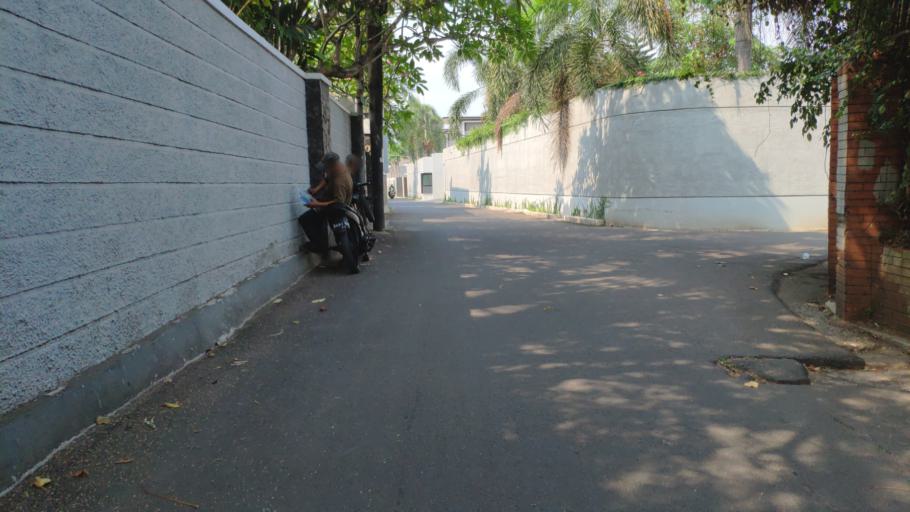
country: ID
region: Jakarta Raya
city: Jakarta
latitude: -6.2726
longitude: 106.8242
